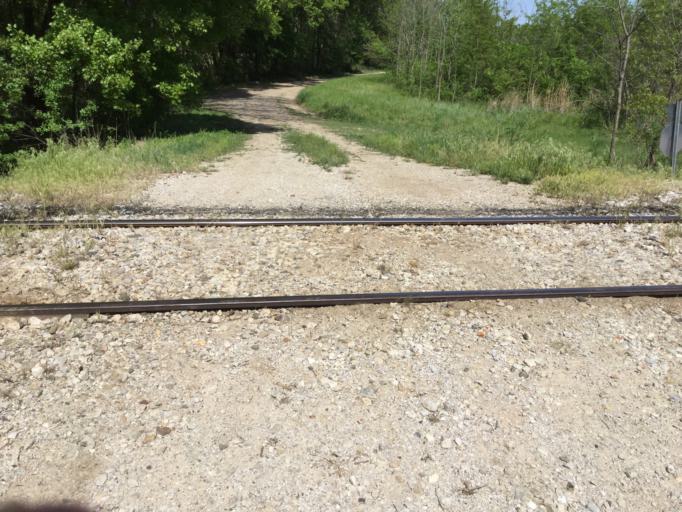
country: US
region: Kansas
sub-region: Montgomery County
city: Cherryvale
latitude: 37.2961
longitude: -95.5782
